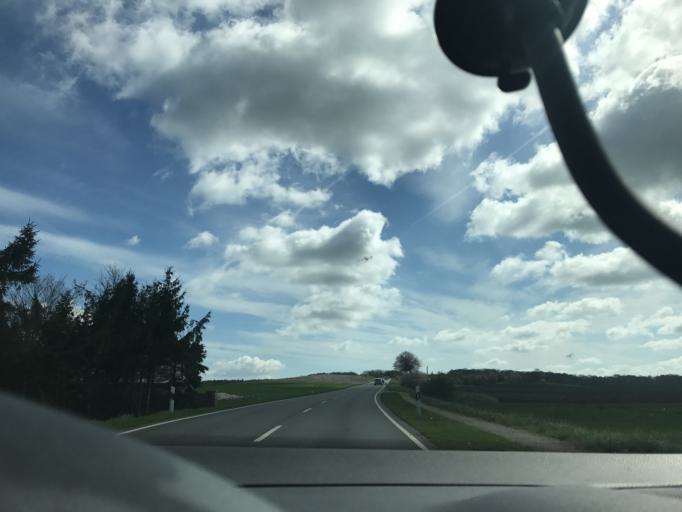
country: DE
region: Lower Saxony
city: Schoppenstedt
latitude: 52.1433
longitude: 10.7898
